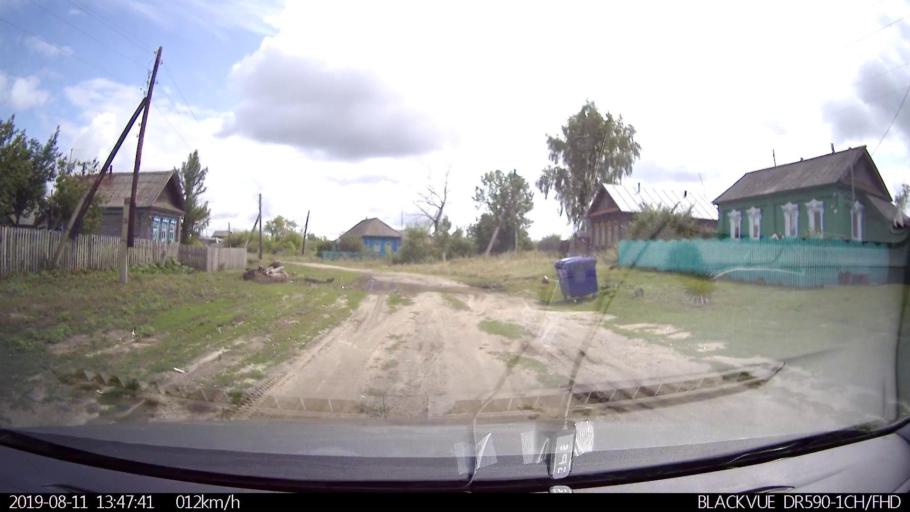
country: RU
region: Ulyanovsk
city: Ignatovka
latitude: 53.8487
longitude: 47.5775
